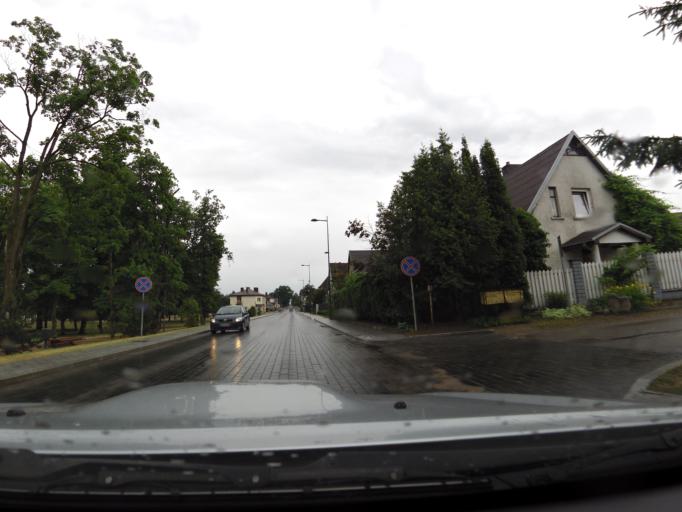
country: LT
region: Marijampoles apskritis
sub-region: Marijampole Municipality
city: Marijampole
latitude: 54.5529
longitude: 23.3449
